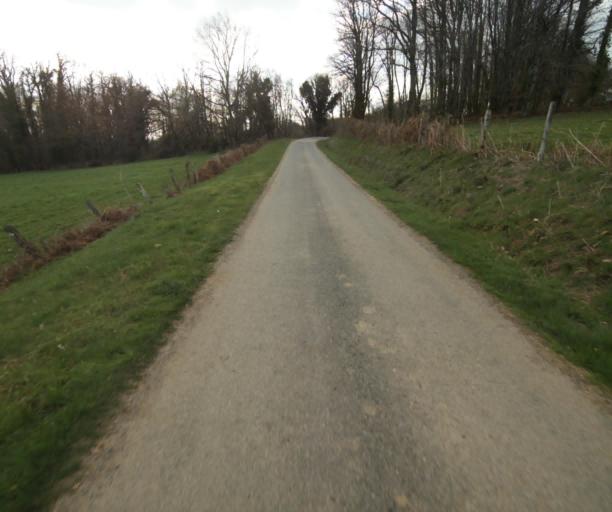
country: FR
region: Limousin
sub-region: Departement de la Correze
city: Saint-Clement
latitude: 45.3626
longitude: 1.6402
